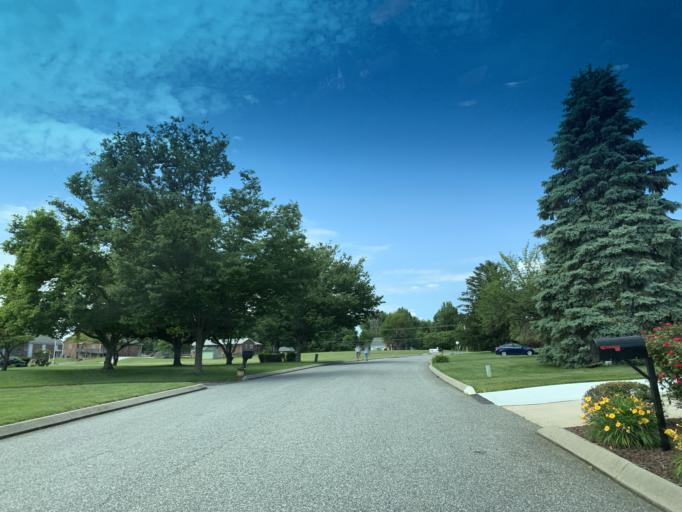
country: US
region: Maryland
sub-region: Harford County
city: Jarrettsville
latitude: 39.6265
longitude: -76.4654
